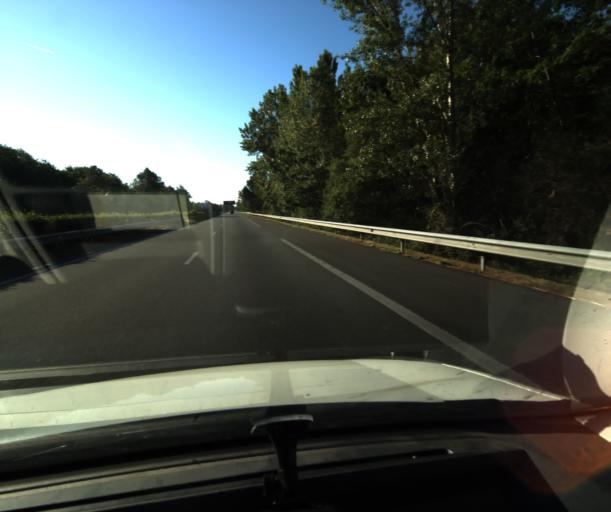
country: FR
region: Midi-Pyrenees
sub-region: Departement du Tarn-et-Garonne
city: Montech
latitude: 43.9631
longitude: 1.2763
